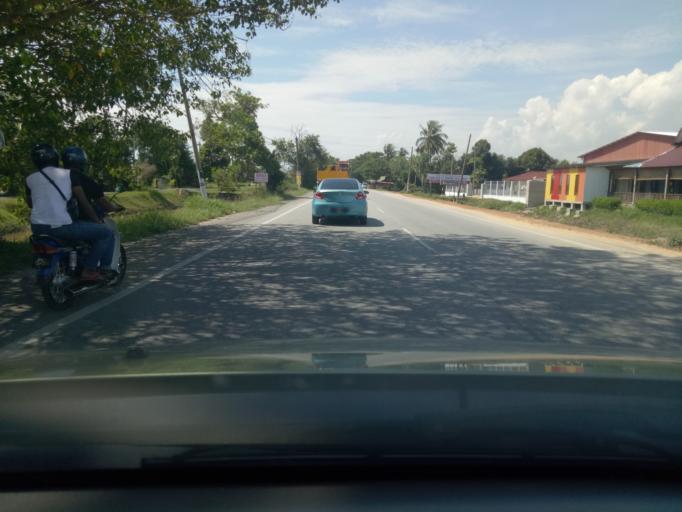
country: MY
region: Kedah
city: Gurun
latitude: 5.9629
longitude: 100.4042
